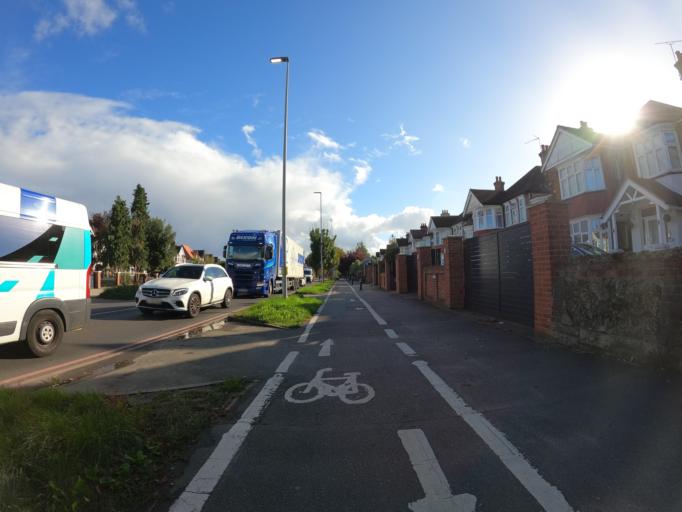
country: GB
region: England
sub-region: Greater London
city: Acton
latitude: 51.5041
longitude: -0.2894
